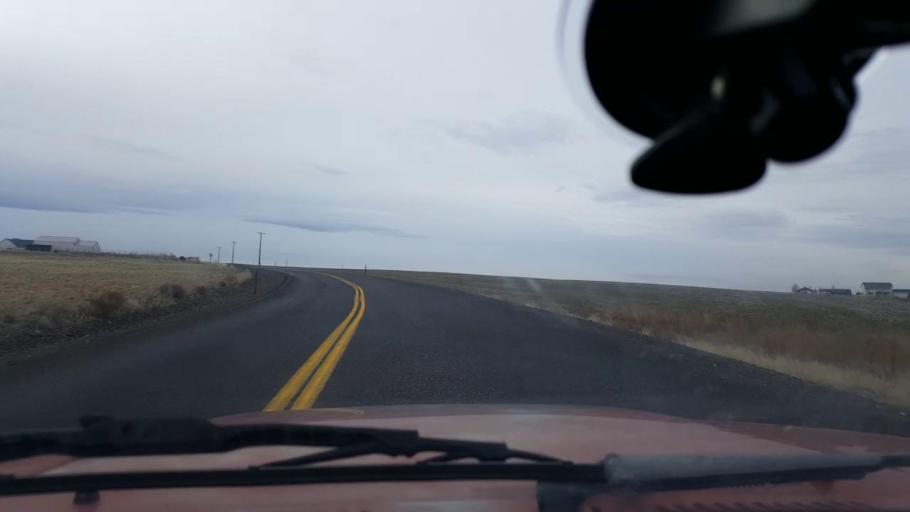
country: US
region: Washington
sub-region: Asotin County
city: Clarkston Heights-Vineland
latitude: 46.3781
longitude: -117.1524
